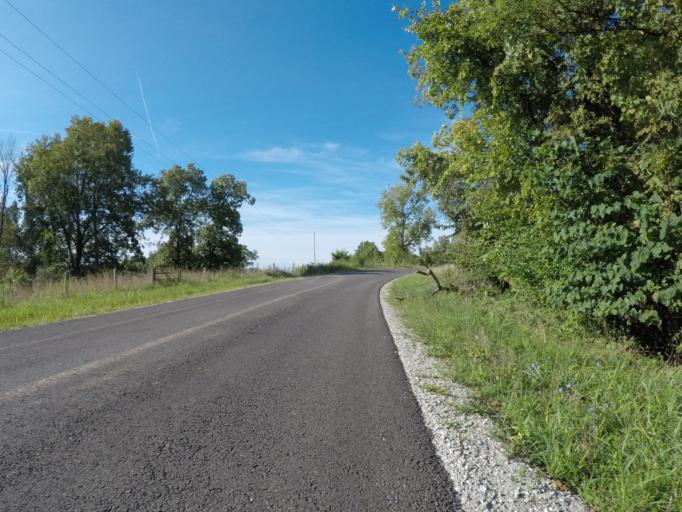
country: US
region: Ohio
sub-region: Lawrence County
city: Burlington
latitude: 38.5228
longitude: -82.5242
